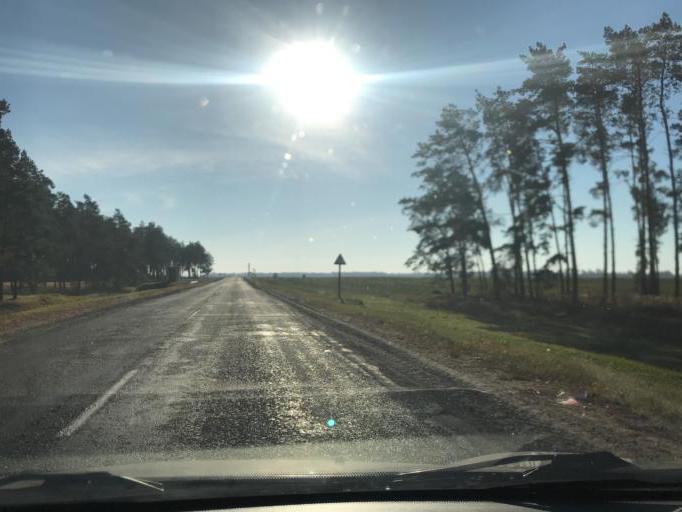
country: BY
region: Gomel
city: Khoyniki
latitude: 51.8135
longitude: 30.0977
